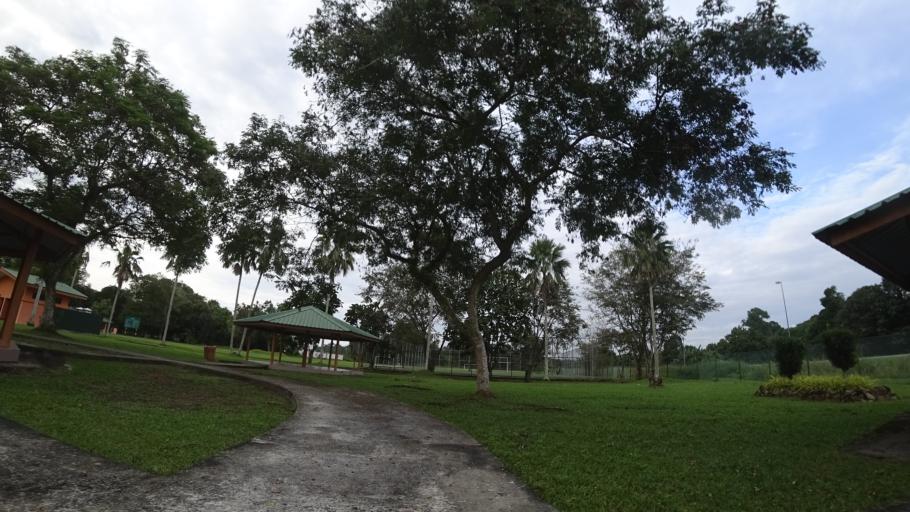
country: BN
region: Brunei and Muara
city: Bandar Seri Begawan
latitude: 4.8080
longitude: 114.8327
